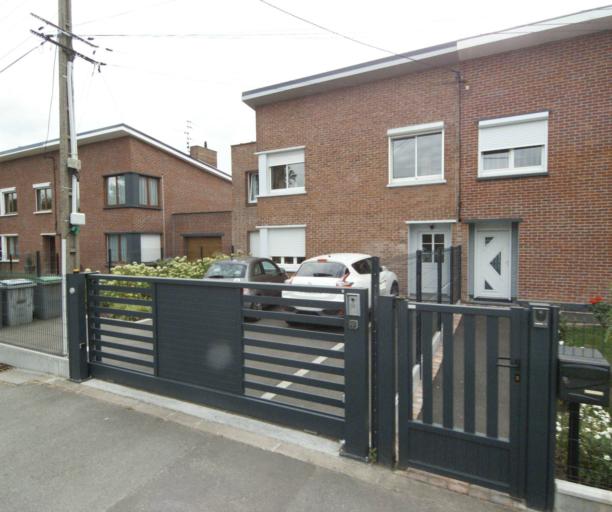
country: FR
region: Nord-Pas-de-Calais
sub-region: Departement du Nord
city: Gruson
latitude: 50.5987
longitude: 3.2011
